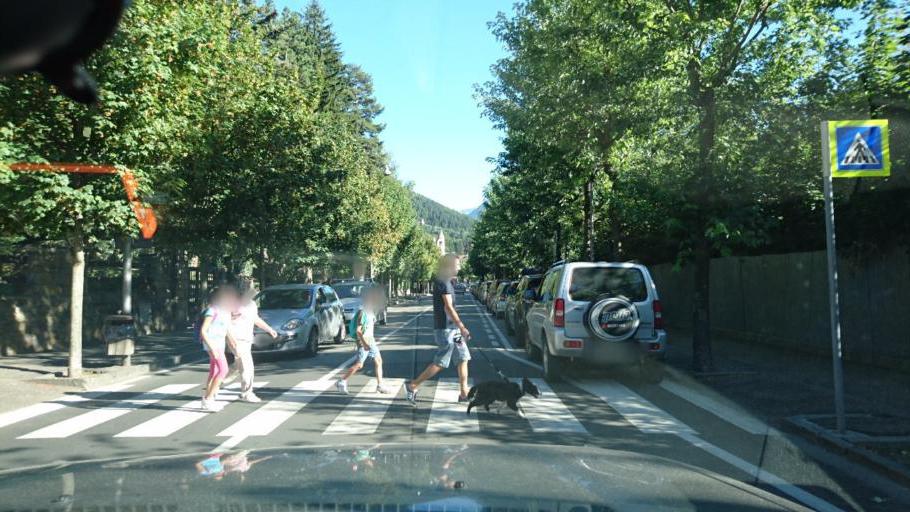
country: IT
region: Aosta Valley
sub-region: Valle d'Aosta
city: Courmayeur
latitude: 45.7950
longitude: 6.9697
